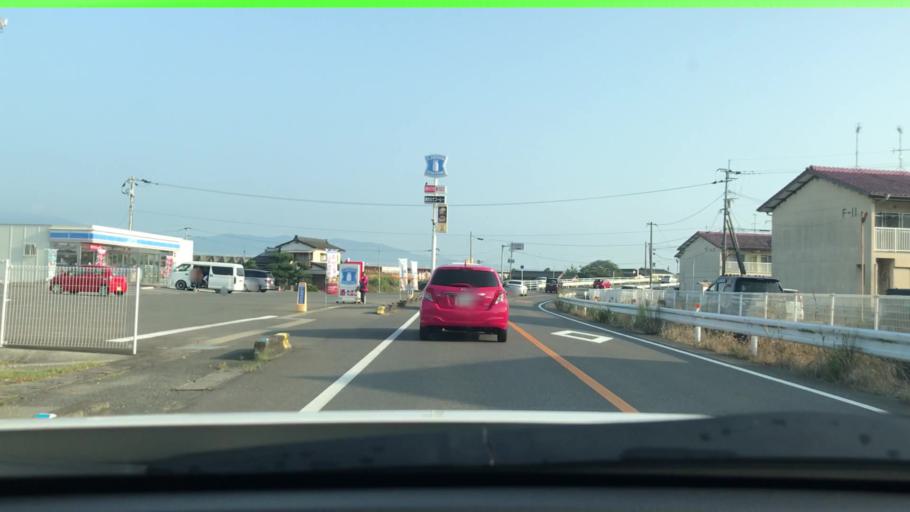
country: JP
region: Saga Prefecture
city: Saga-shi
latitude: 33.1980
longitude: 130.1934
